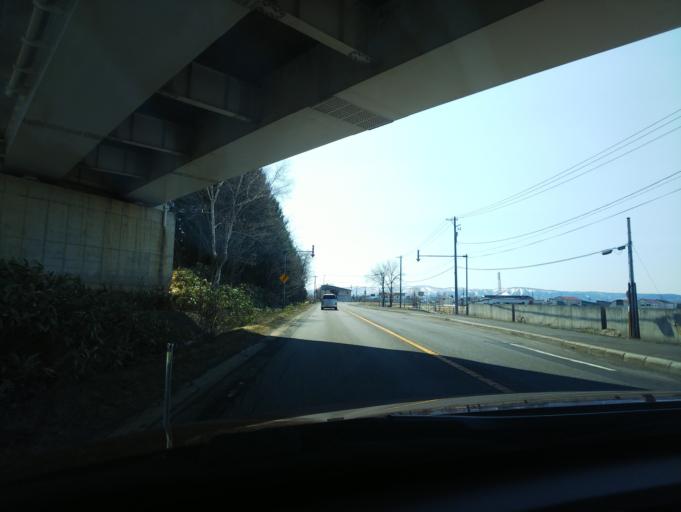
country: JP
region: Hokkaido
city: Nayoro
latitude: 44.2995
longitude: 142.4294
